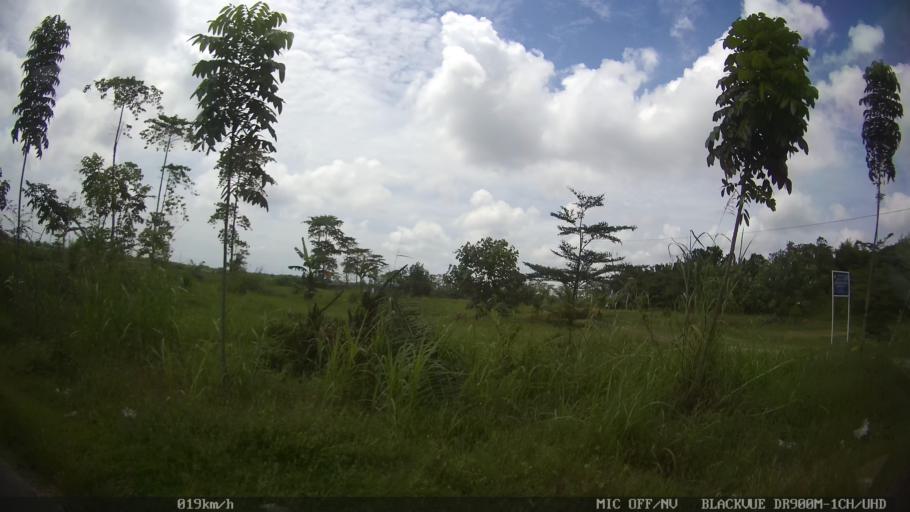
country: ID
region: North Sumatra
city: Percut
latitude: 3.6200
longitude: 98.7695
